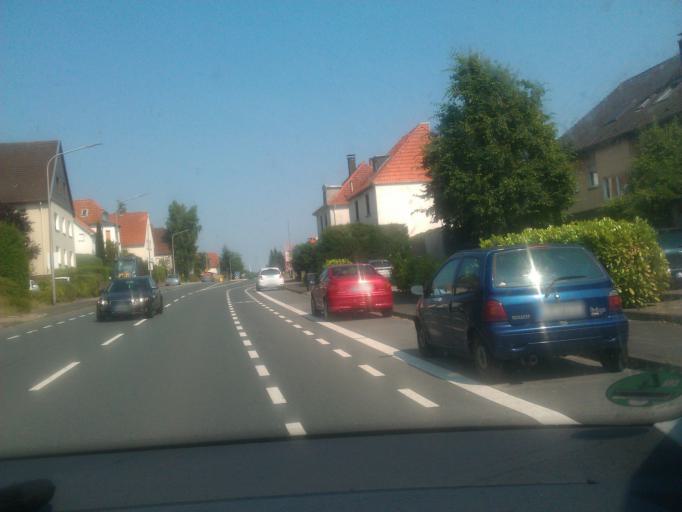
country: DE
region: North Rhine-Westphalia
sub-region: Regierungsbezirk Detmold
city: Lemgo
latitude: 52.0287
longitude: 8.8768
